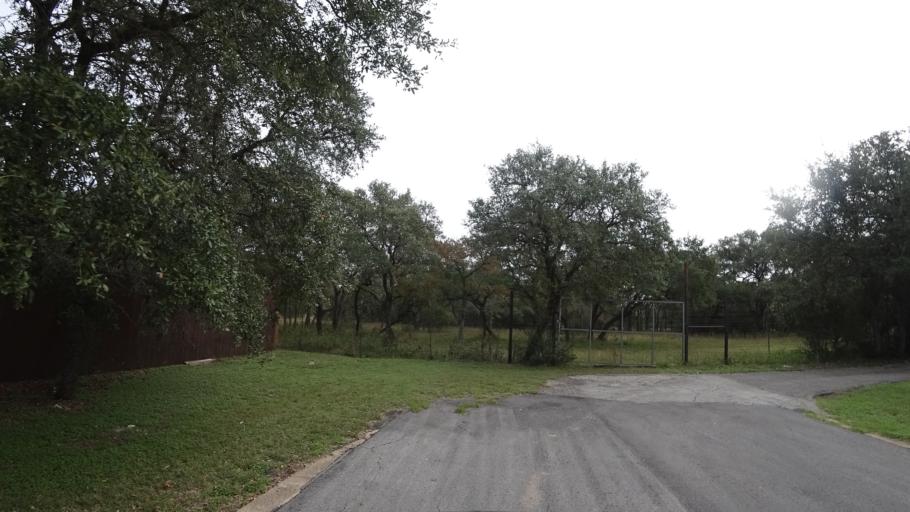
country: US
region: Texas
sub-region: Travis County
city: Shady Hollow
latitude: 30.1403
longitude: -97.8808
